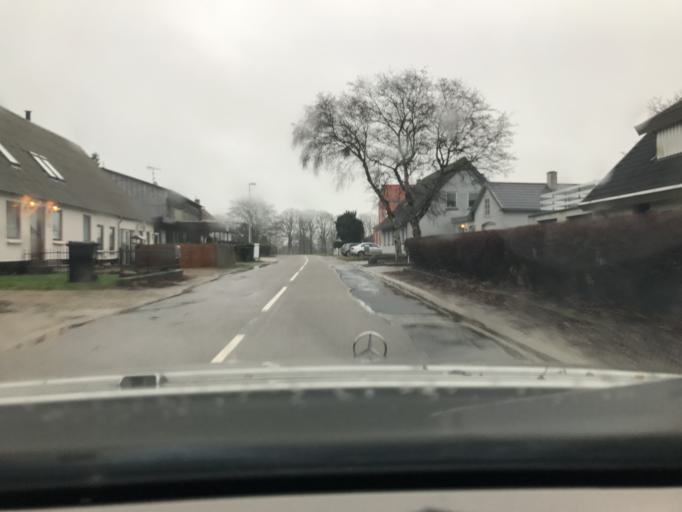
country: DK
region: South Denmark
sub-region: Sonderborg Kommune
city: Horuphav
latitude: 54.8937
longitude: 10.0280
